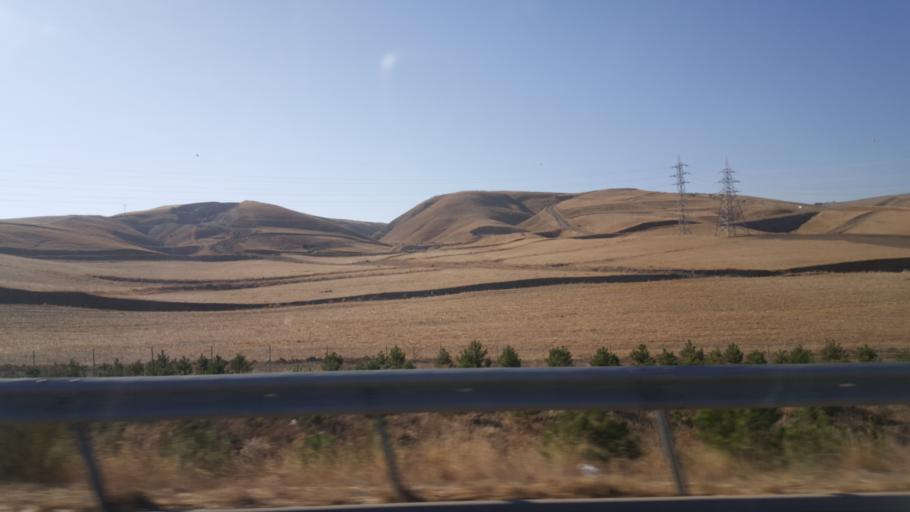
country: TR
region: Ankara
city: Mamak
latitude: 39.8716
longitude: 32.9214
